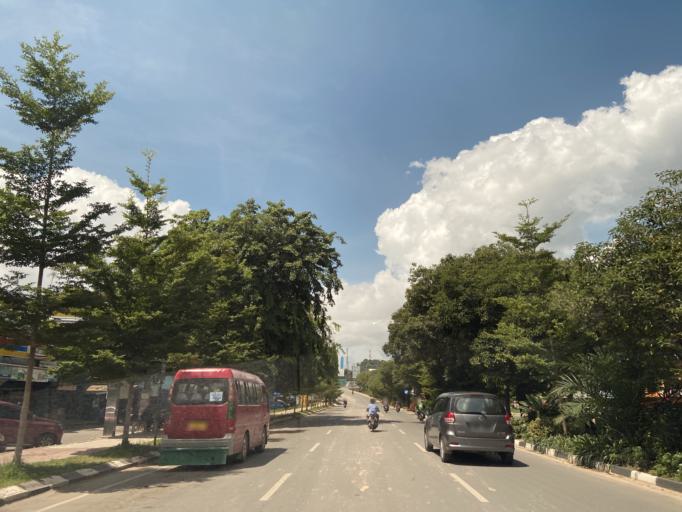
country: SG
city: Singapore
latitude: 1.1451
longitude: 104.0114
